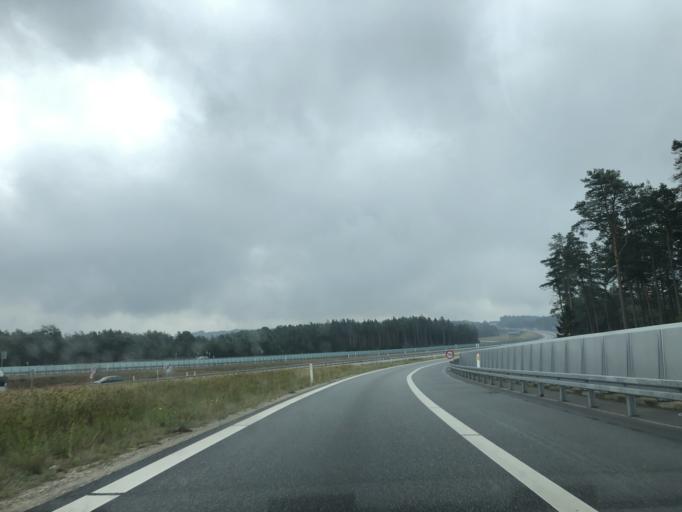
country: DK
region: Central Jutland
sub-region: Silkeborg Kommune
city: Svejbaek
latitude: 56.1680
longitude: 9.6017
